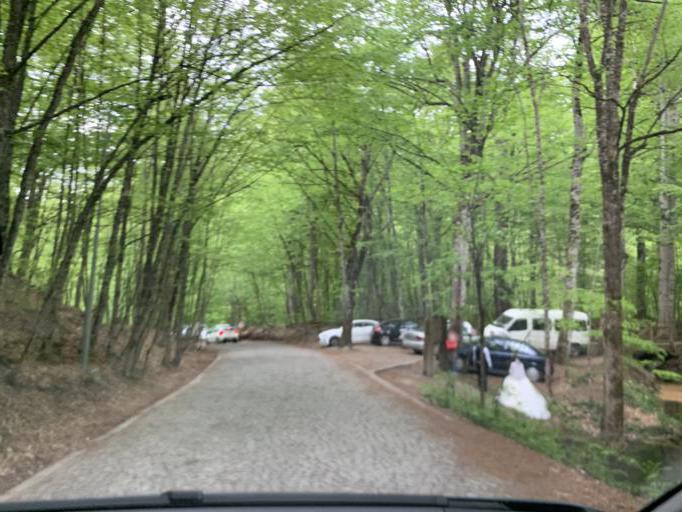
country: TR
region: Zonguldak
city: Egerci
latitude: 40.9386
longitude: 31.7429
